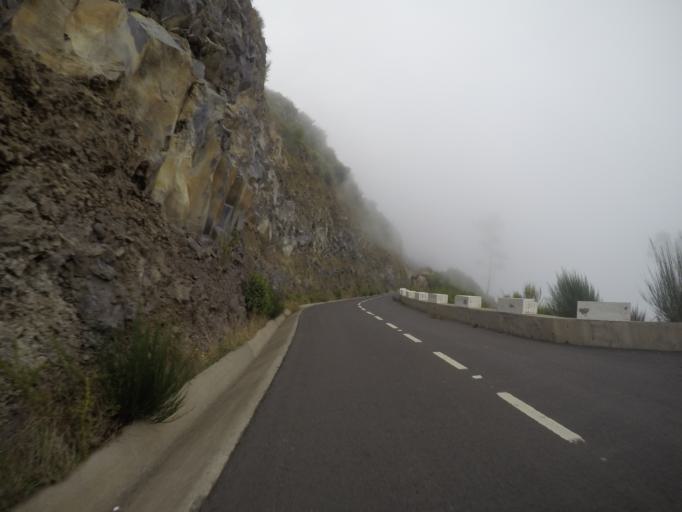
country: PT
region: Madeira
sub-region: Camara de Lobos
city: Curral das Freiras
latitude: 32.7090
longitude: -16.9549
